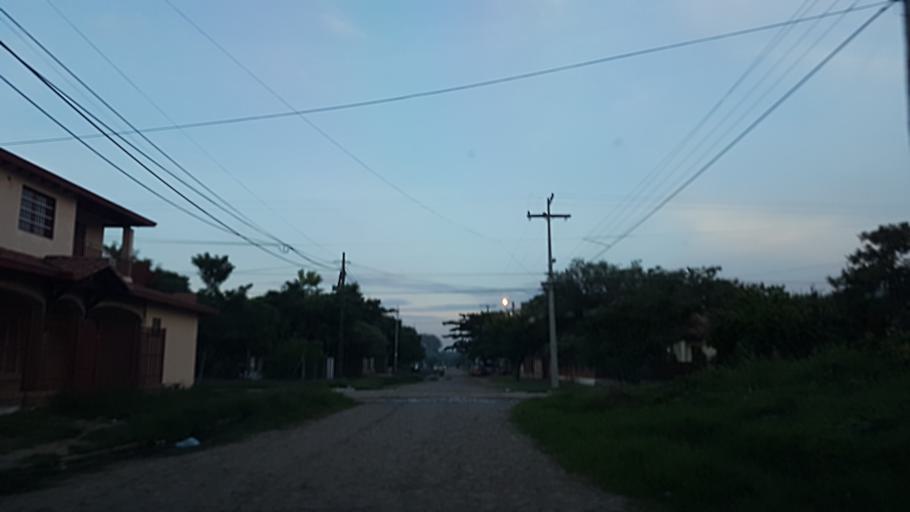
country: PY
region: Central
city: Colonia Mariano Roque Alonso
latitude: -25.2093
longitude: -57.5364
